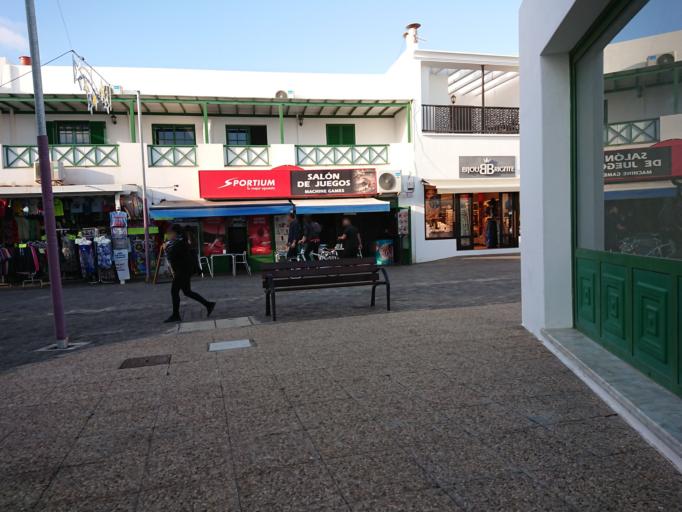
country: ES
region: Canary Islands
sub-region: Provincia de Las Palmas
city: Playa Blanca
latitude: 28.8617
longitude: -13.8319
